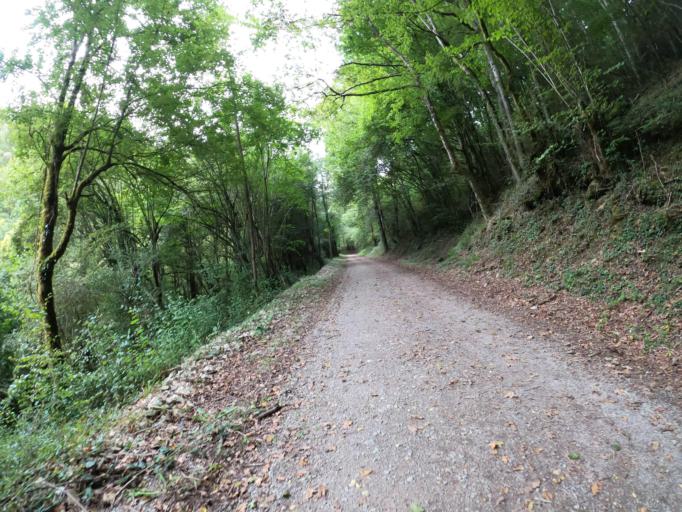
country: ES
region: Navarre
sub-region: Provincia de Navarra
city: Lekunberri
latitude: 42.9829
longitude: -1.8681
